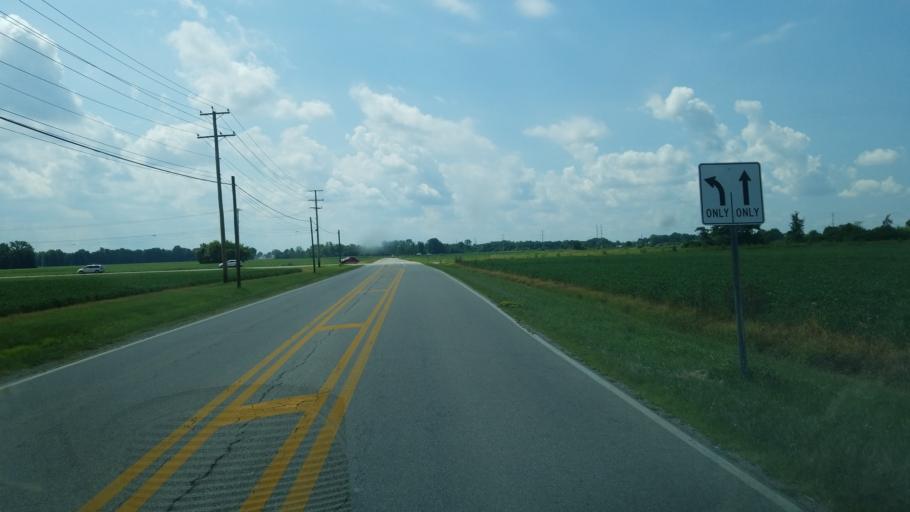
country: US
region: Ohio
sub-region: Delaware County
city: Lewis Center
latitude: 40.2184
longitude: -83.0075
